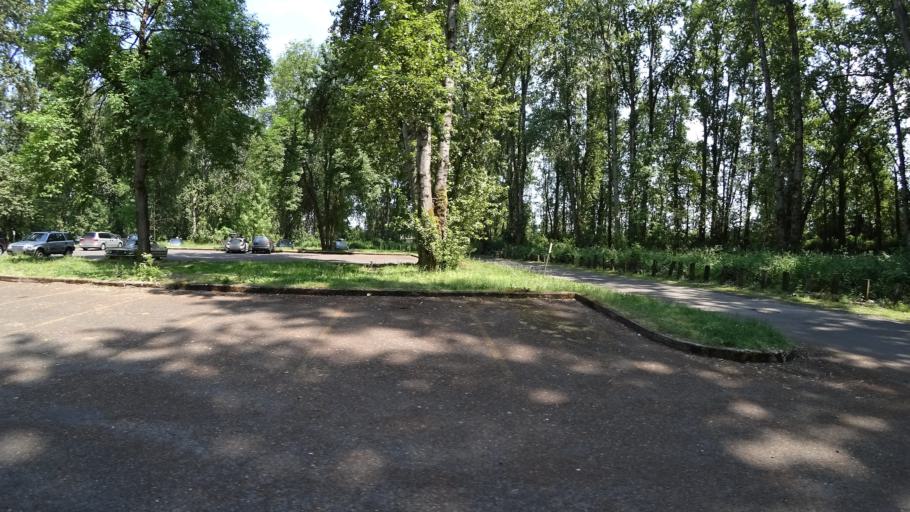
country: US
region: Washington
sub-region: Clark County
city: Felida
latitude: 45.6462
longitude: -122.7622
